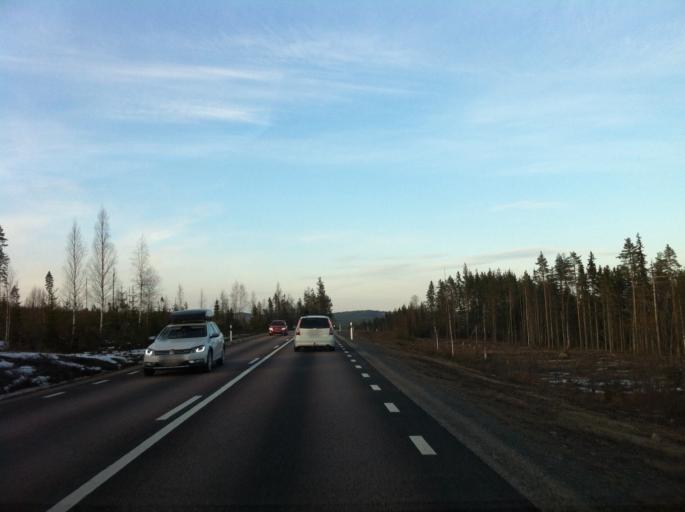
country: SE
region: Vaermland
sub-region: Filipstads Kommun
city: Lesjofors
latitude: 60.0703
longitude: 14.1374
